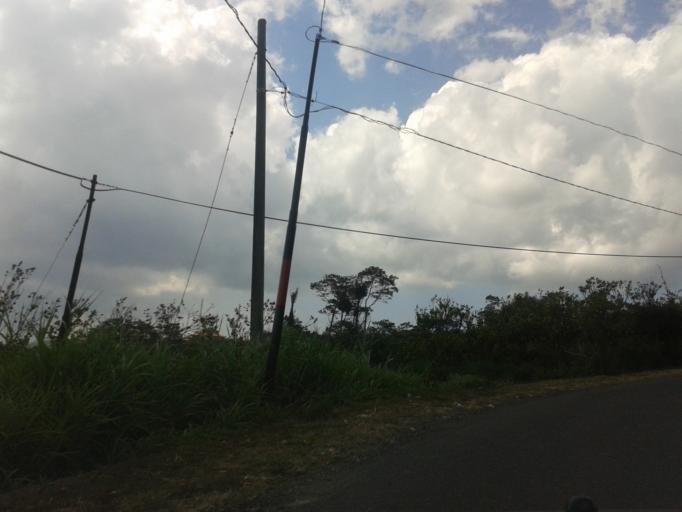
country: ID
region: Bali
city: Banjar Kedisan
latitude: -8.2800
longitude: 115.3503
